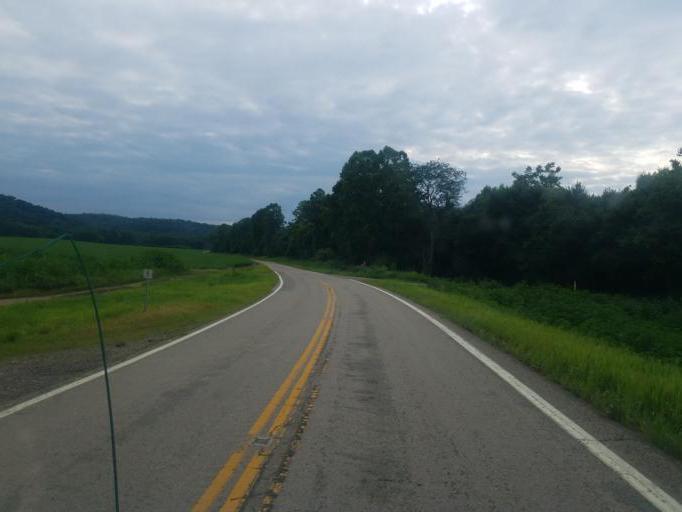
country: US
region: Ohio
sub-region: Knox County
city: Oak Hill
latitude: 40.3555
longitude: -82.1060
